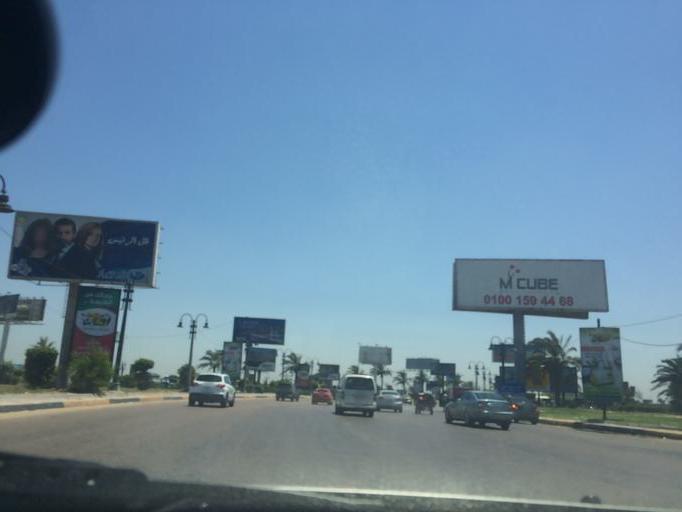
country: EG
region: Alexandria
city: Alexandria
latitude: 31.1673
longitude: 29.9352
